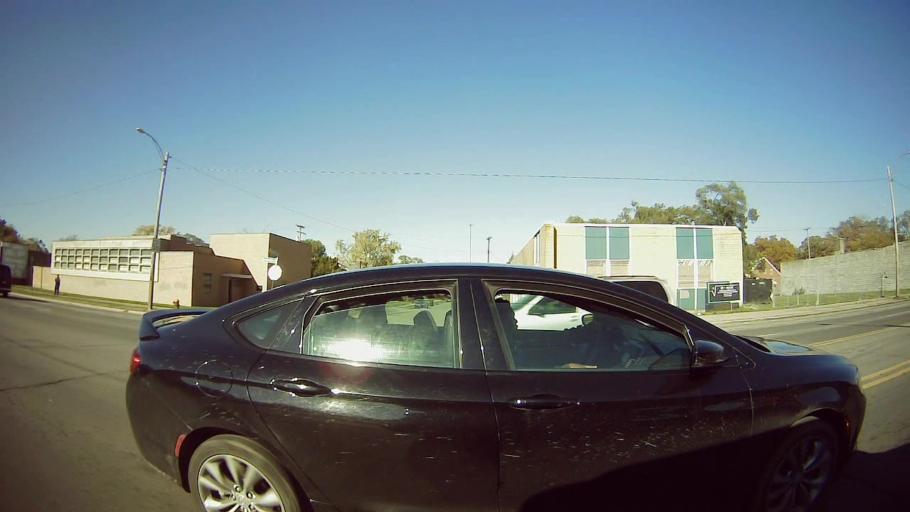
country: US
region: Michigan
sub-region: Oakland County
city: Oak Park
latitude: 42.4312
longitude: -83.1717
